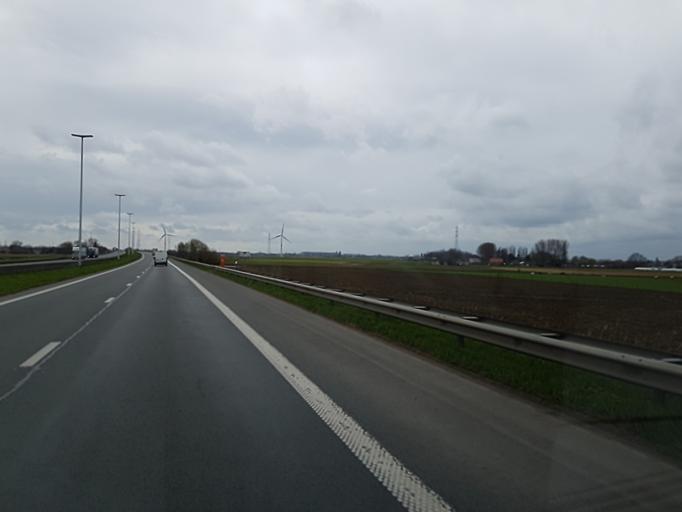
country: BE
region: Wallonia
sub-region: Province du Hainaut
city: Estaimpuis
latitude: 50.6956
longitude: 3.2939
